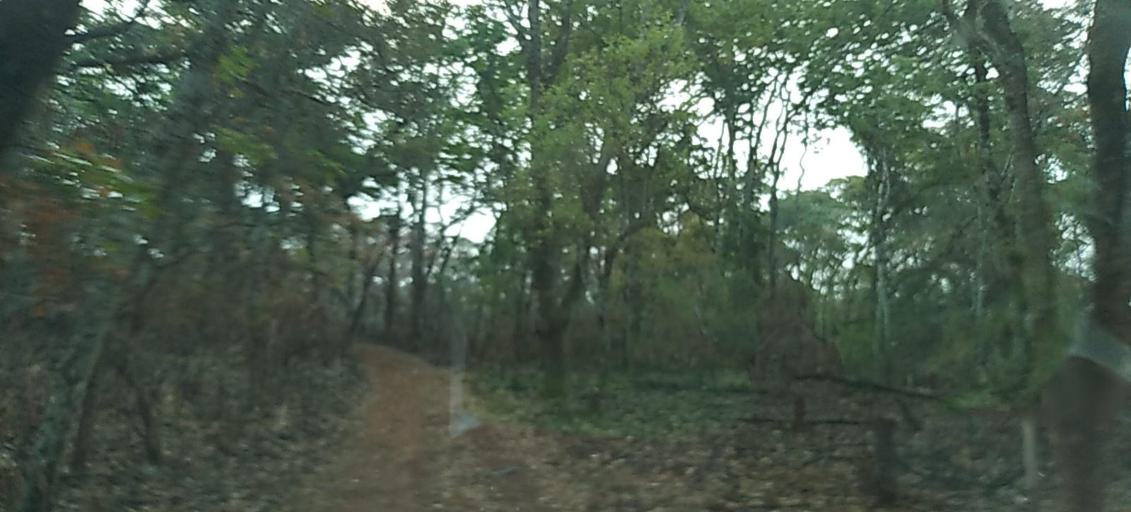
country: ZM
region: North-Western
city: Solwezi
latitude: -12.0444
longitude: 26.0112
